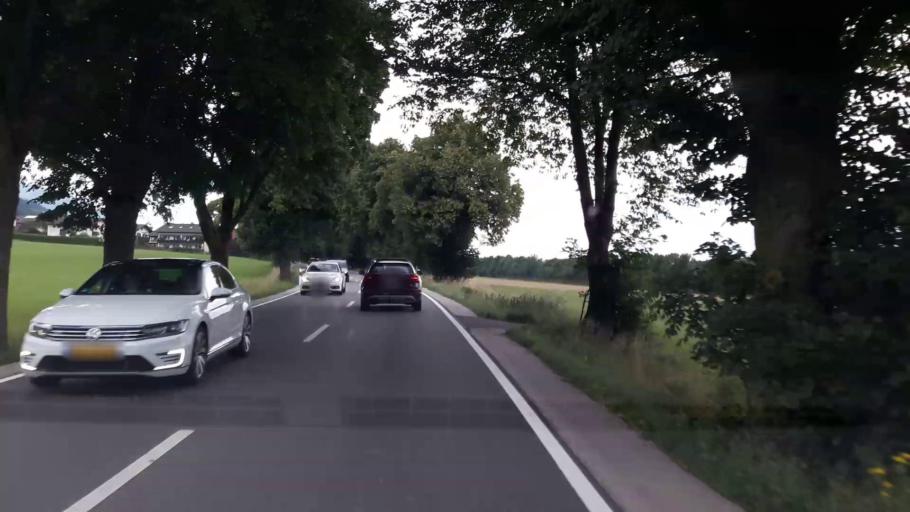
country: DE
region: Bavaria
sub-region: Upper Bavaria
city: Anger
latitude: 47.7791
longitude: 12.8764
